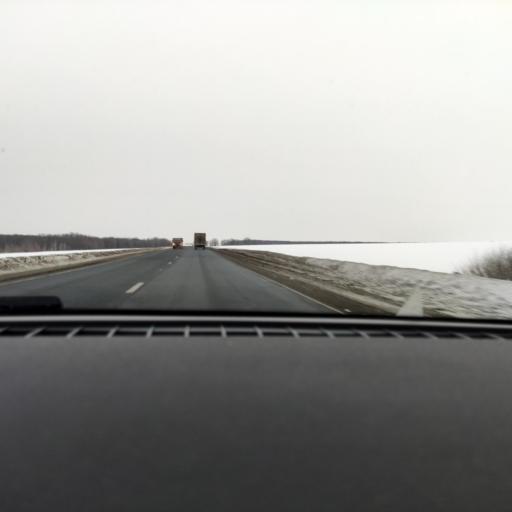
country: RU
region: Samara
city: Petra-Dubrava
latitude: 53.3155
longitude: 50.4564
